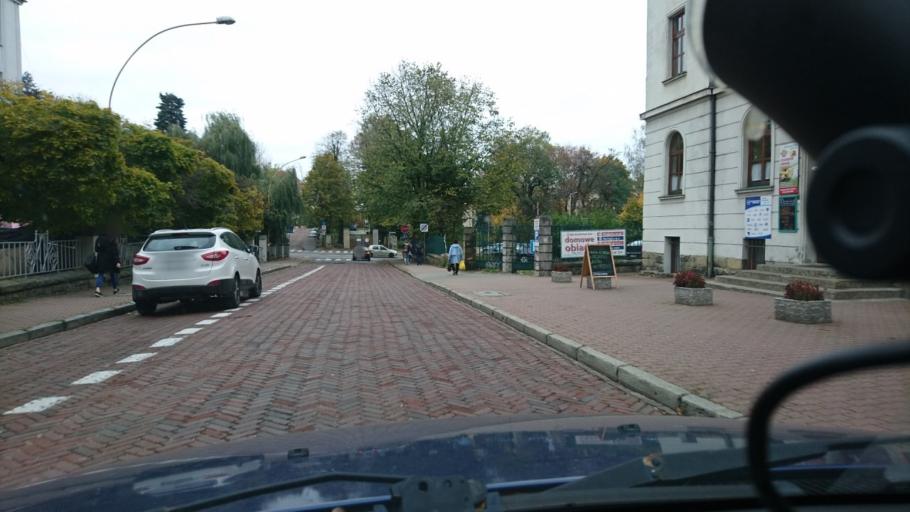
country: PL
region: Silesian Voivodeship
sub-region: Bielsko-Biala
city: Bielsko-Biala
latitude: 49.8278
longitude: 19.0411
